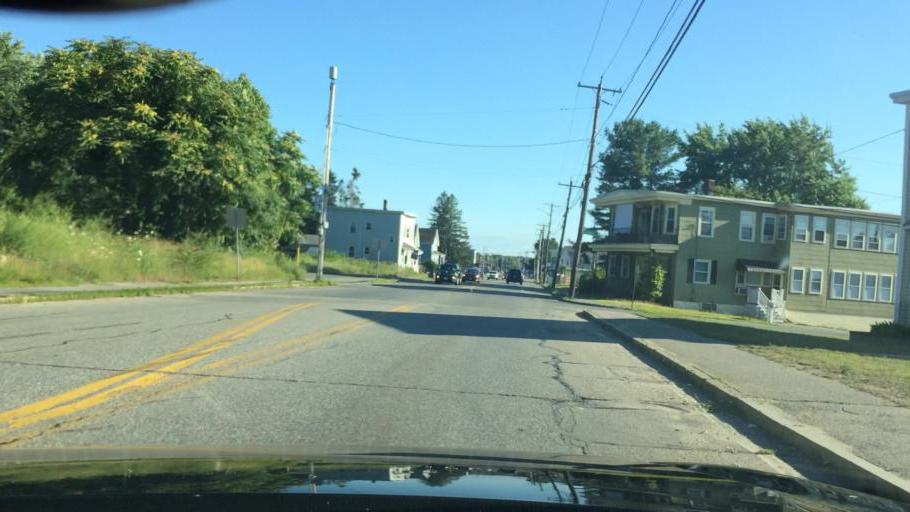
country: US
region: Massachusetts
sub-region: Essex County
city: North Andover
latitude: 42.7465
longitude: -71.1300
